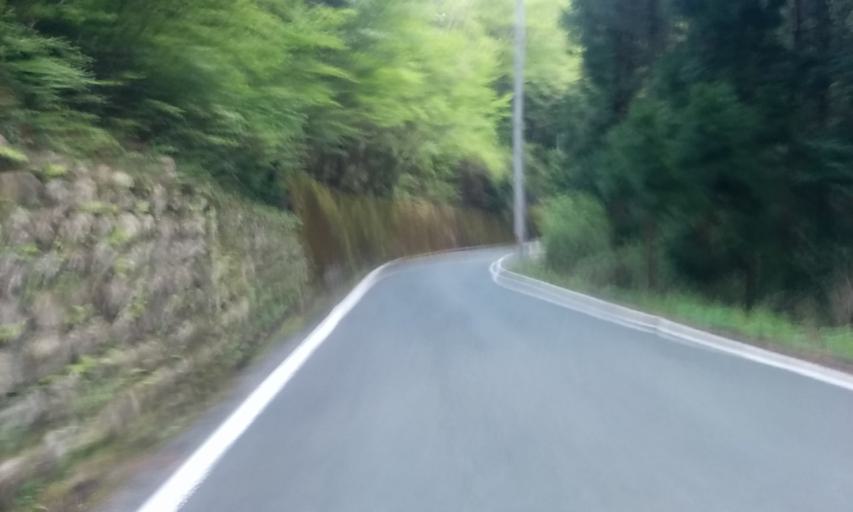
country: JP
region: Ehime
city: Saijo
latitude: 33.8014
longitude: 133.2790
